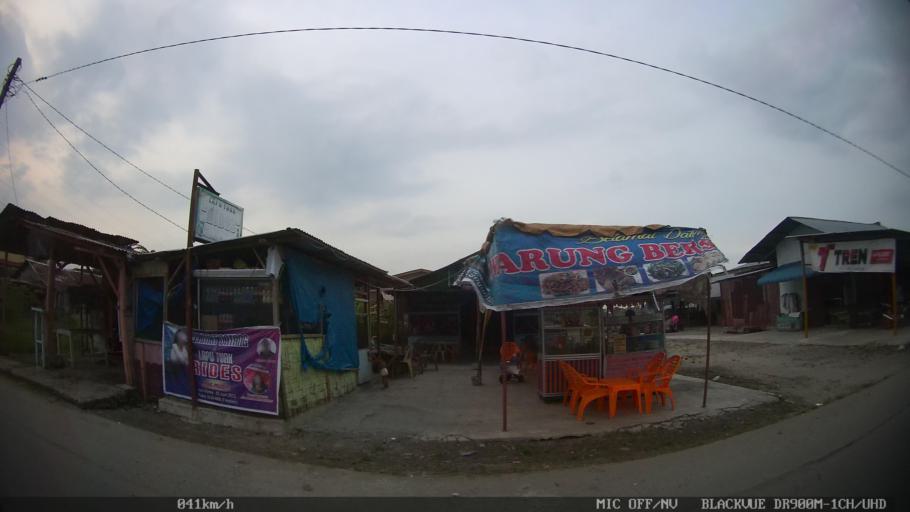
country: ID
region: North Sumatra
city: Sunggal
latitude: 3.5611
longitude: 98.5929
